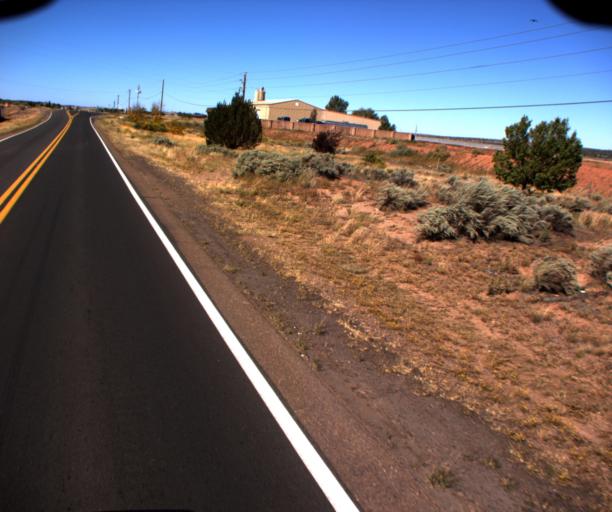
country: US
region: Arizona
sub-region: Navajo County
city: Snowflake
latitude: 34.5133
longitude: -110.0935
